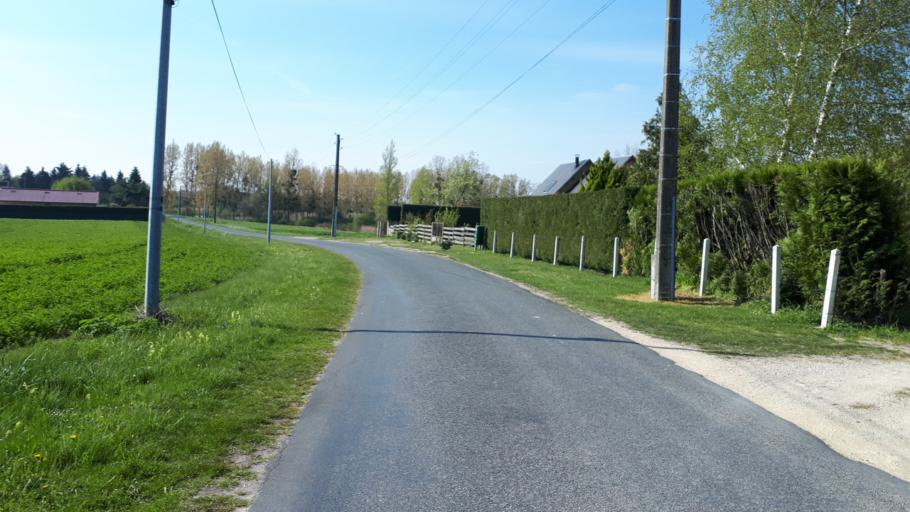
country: FR
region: Centre
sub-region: Departement du Loir-et-Cher
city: Contres
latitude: 47.3848
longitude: 1.3779
